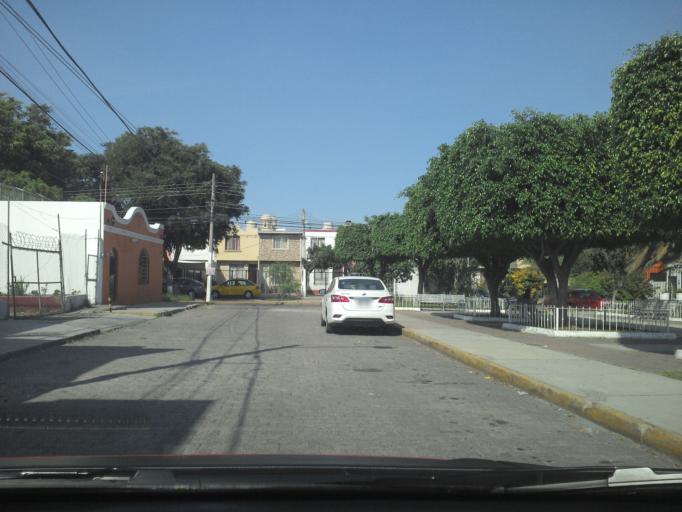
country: MX
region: Jalisco
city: Guadalajara
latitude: 20.6476
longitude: -103.4405
